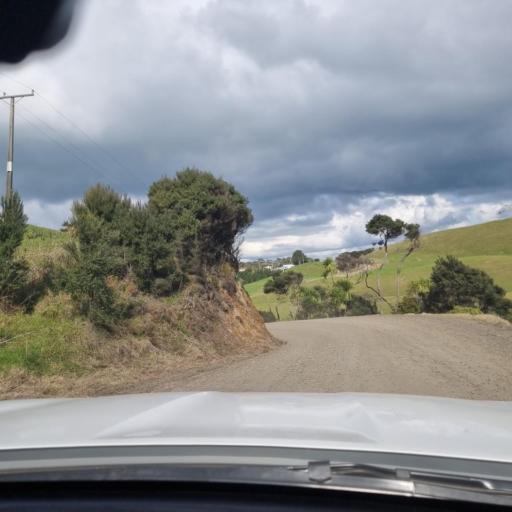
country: NZ
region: Auckland
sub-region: Auckland
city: Wellsford
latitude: -36.3484
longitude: 174.1702
